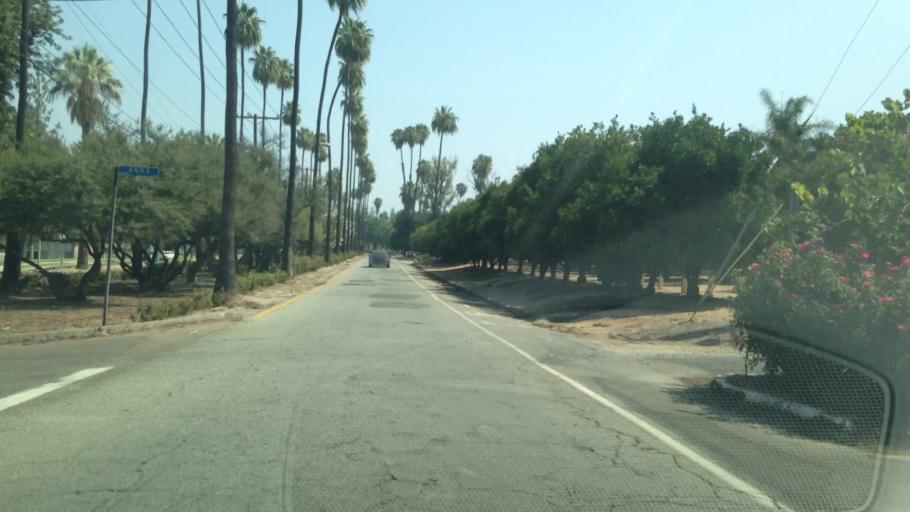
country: US
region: California
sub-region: Riverside County
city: Riverside
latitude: 33.9417
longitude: -117.3725
